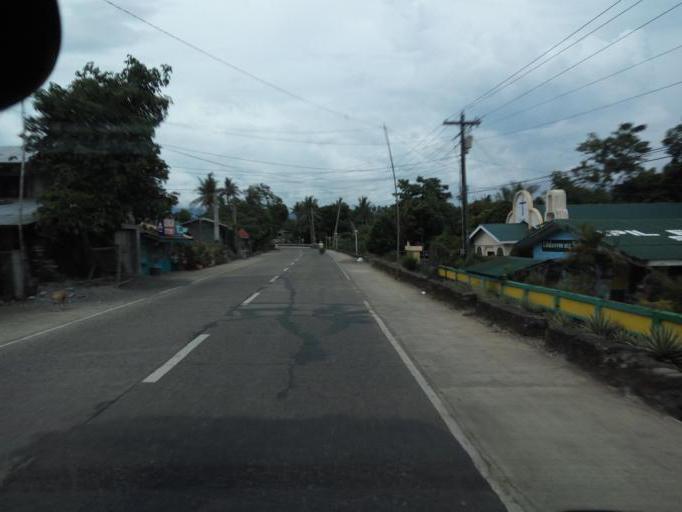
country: PH
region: Cagayan Valley
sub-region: Province of Cagayan
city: Tapel
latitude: 18.3119
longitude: 122.0474
